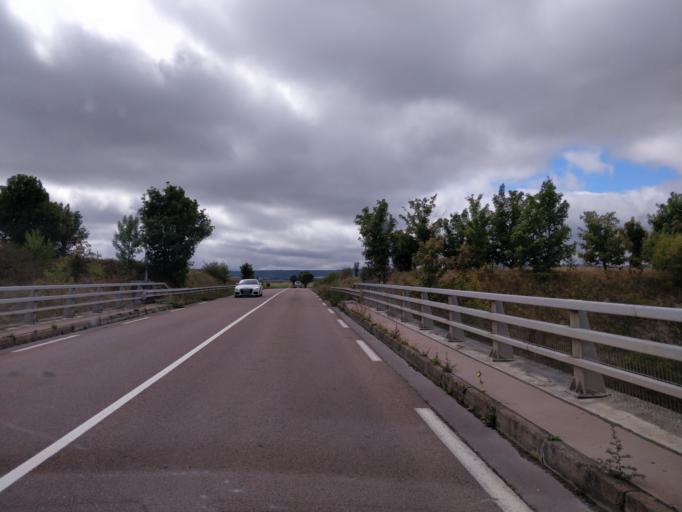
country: FR
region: Champagne-Ardenne
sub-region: Departement de l'Aube
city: Saint-Pouange
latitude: 48.2360
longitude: 4.0195
